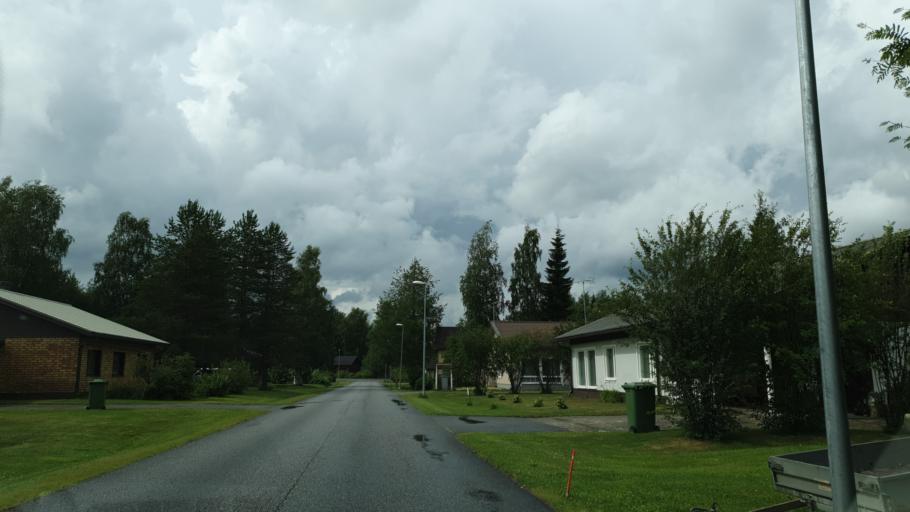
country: FI
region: Kainuu
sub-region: Kehys-Kainuu
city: Kuhmo
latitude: 64.1187
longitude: 29.5070
